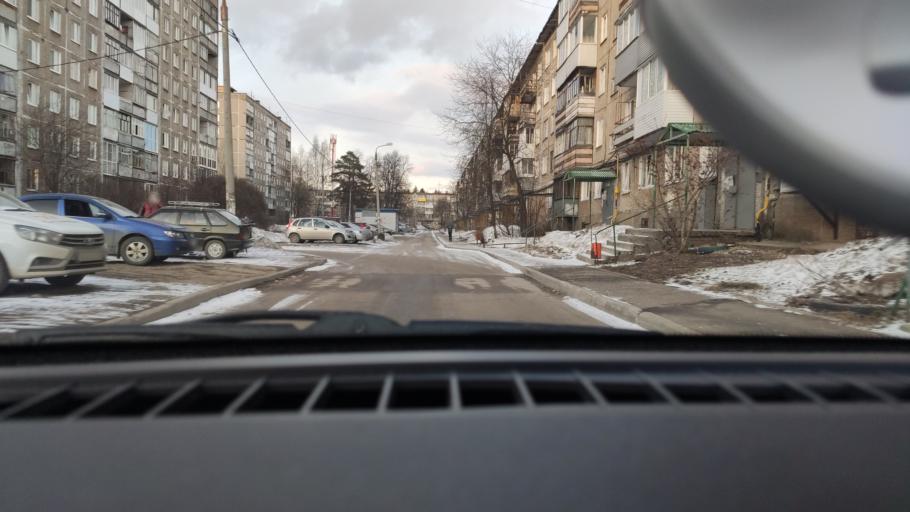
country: RU
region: Perm
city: Perm
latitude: 58.0860
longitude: 56.4080
